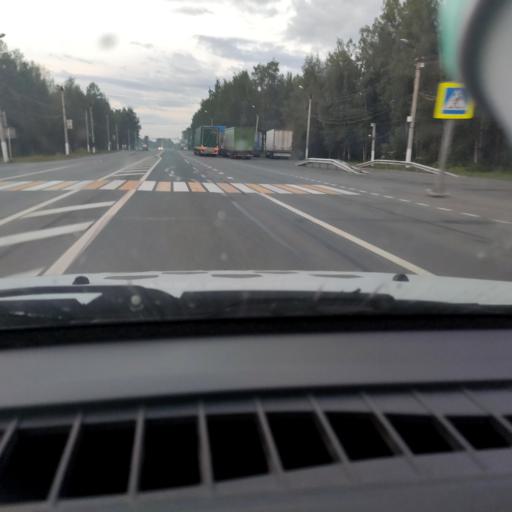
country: RU
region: Kirov
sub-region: Kirovo-Chepetskiy Rayon
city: Kirov
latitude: 58.6797
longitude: 49.6458
